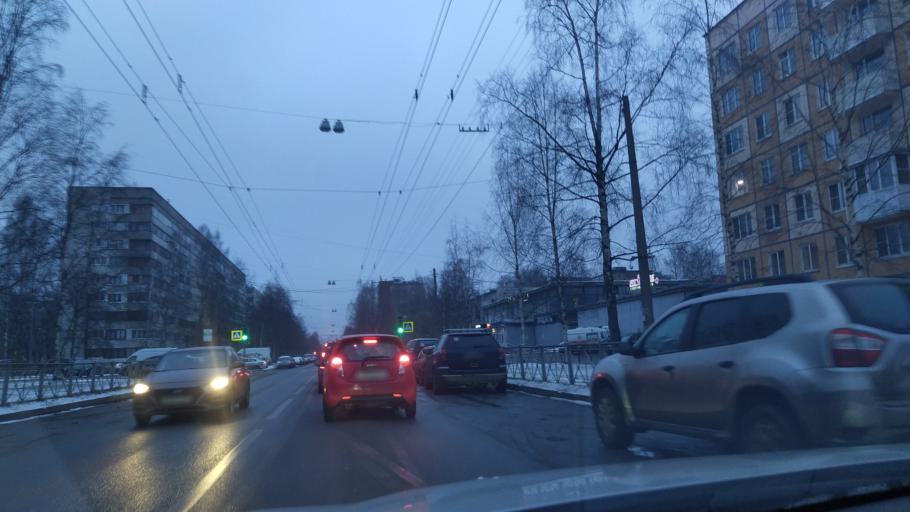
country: RU
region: Leningrad
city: Akademicheskoe
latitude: 60.0118
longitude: 30.4099
